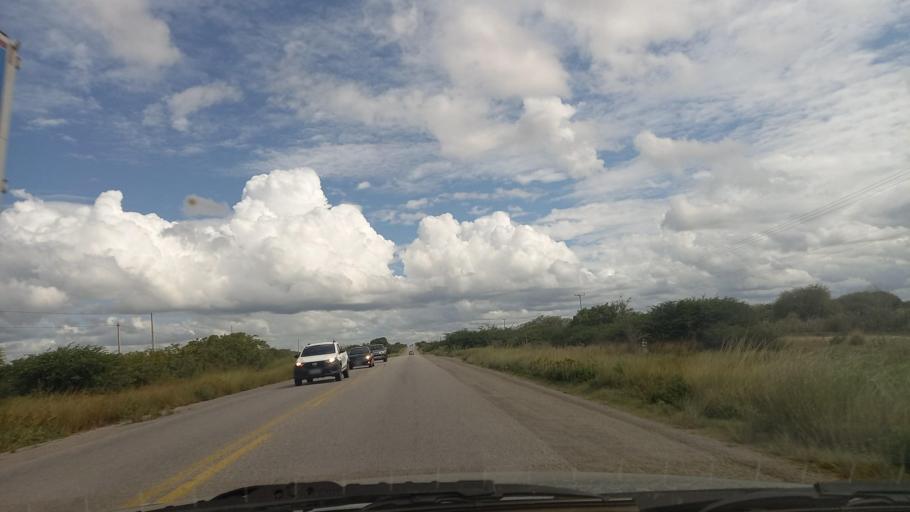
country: BR
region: Pernambuco
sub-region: Cachoeirinha
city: Cachoeirinha
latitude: -8.4348
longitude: -36.2022
